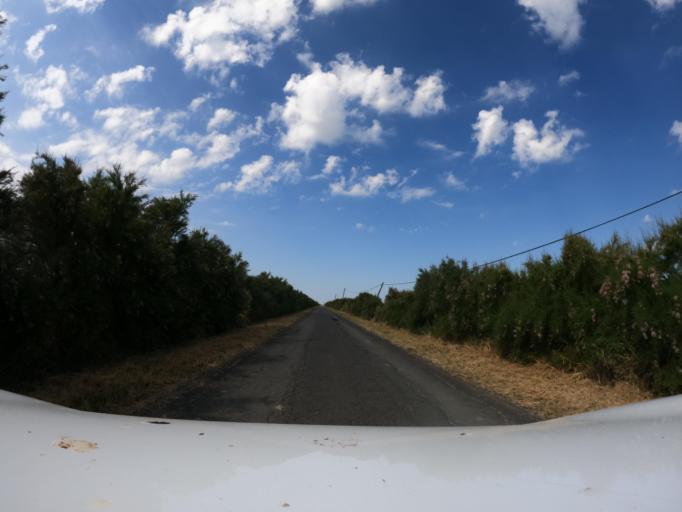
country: FR
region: Poitou-Charentes
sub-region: Departement de la Charente-Maritime
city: Charron
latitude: 46.3306
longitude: -1.1428
